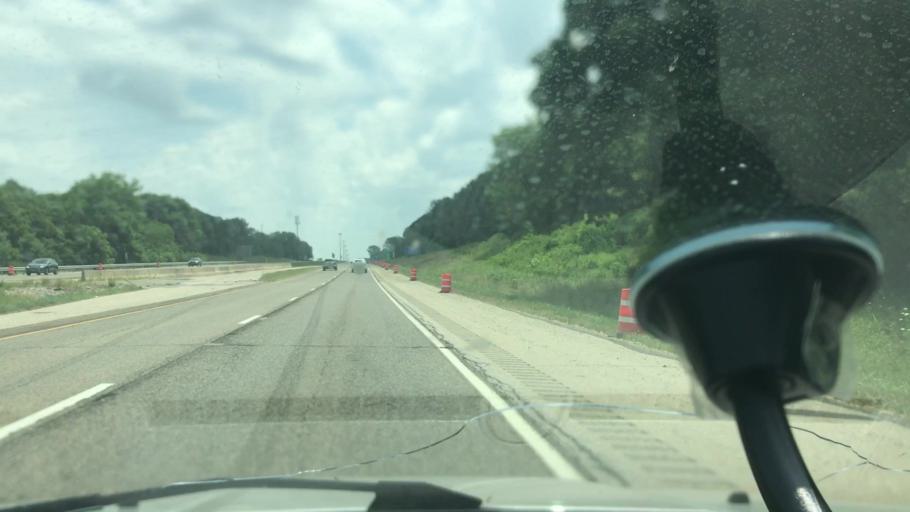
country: US
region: Illinois
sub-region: Peoria County
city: West Peoria
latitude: 40.7394
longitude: -89.6480
